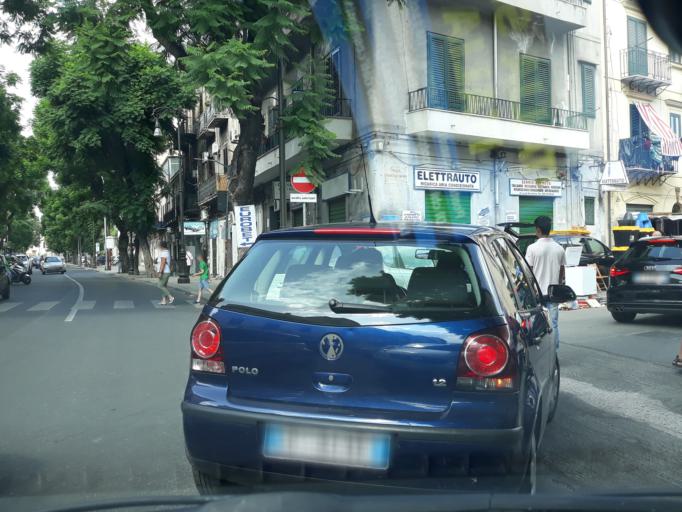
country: IT
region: Sicily
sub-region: Palermo
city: Palermo
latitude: 38.1089
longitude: 13.3594
